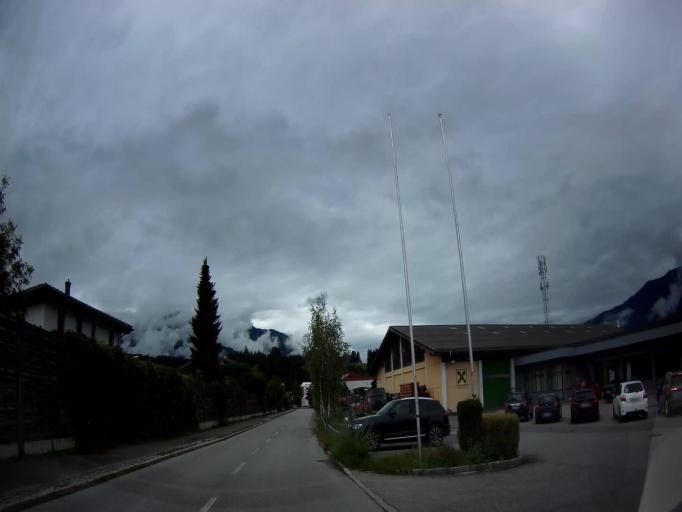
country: AT
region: Salzburg
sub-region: Politischer Bezirk Zell am See
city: Saalfelden am Steinernen Meer
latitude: 47.4237
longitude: 12.8325
